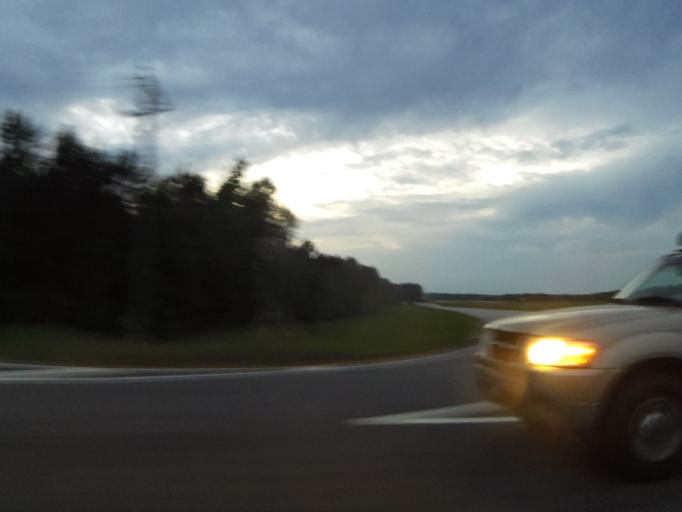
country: US
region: Georgia
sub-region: McDuffie County
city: Thomson
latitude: 33.5278
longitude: -82.5055
